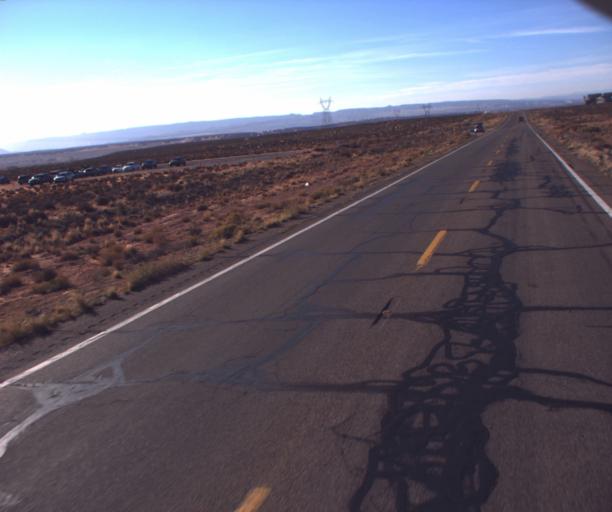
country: US
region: Arizona
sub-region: Coconino County
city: LeChee
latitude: 36.8883
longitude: -111.3649
